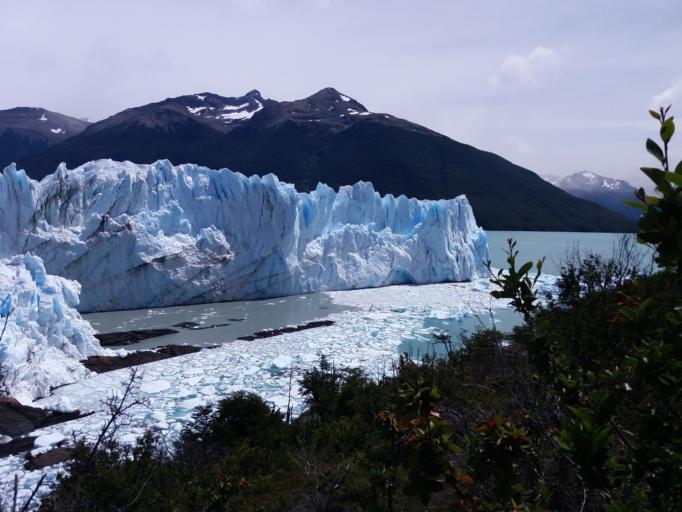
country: AR
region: Santa Cruz
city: El Calafate
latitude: -50.4722
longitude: -73.0336
